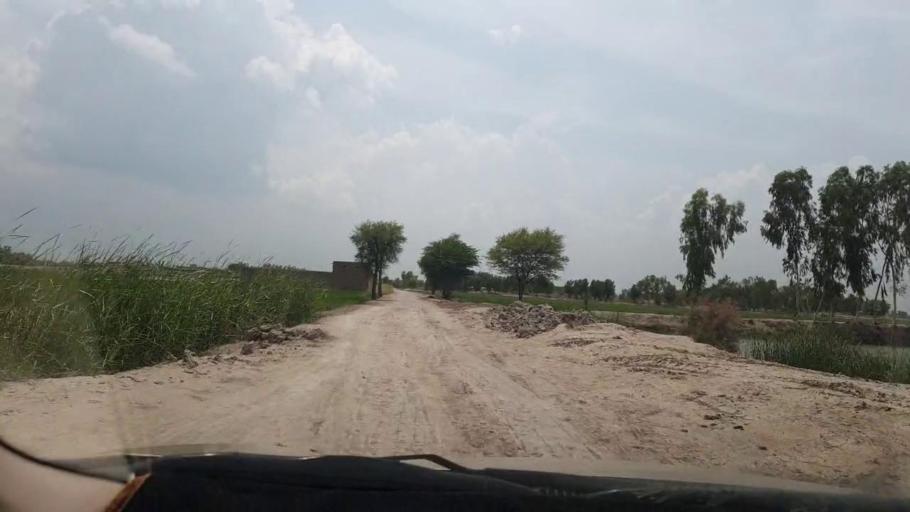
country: PK
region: Sindh
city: Larkana
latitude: 27.6188
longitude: 68.1550
